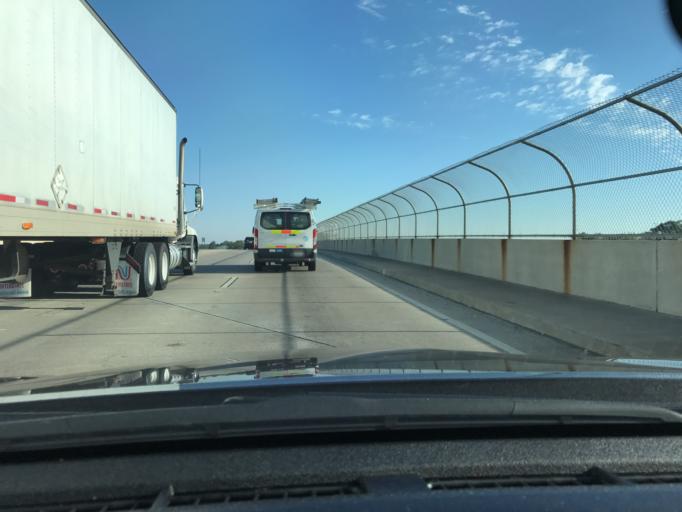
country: US
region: Georgia
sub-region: Clayton County
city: Forest Park
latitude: 33.6261
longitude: -84.3844
